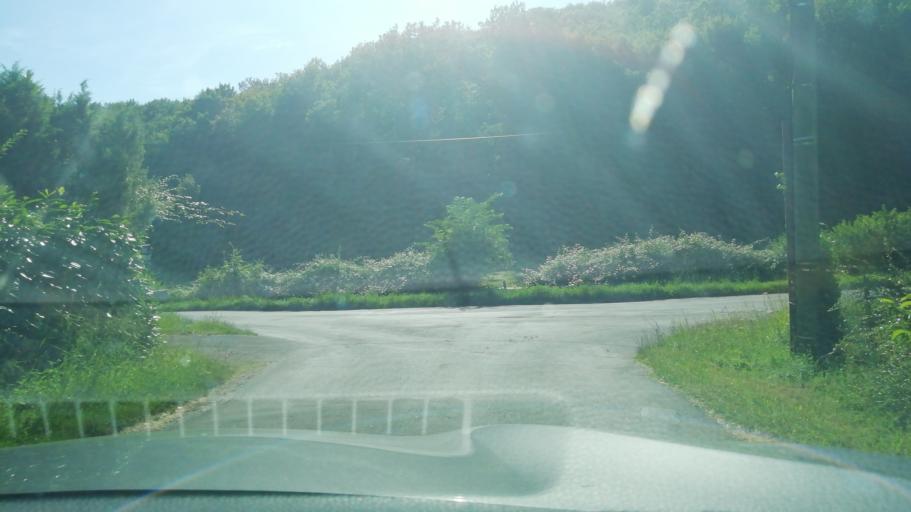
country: FR
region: Aquitaine
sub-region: Departement de la Dordogne
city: Sarlat-la-Caneda
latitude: 44.8613
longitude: 1.2245
